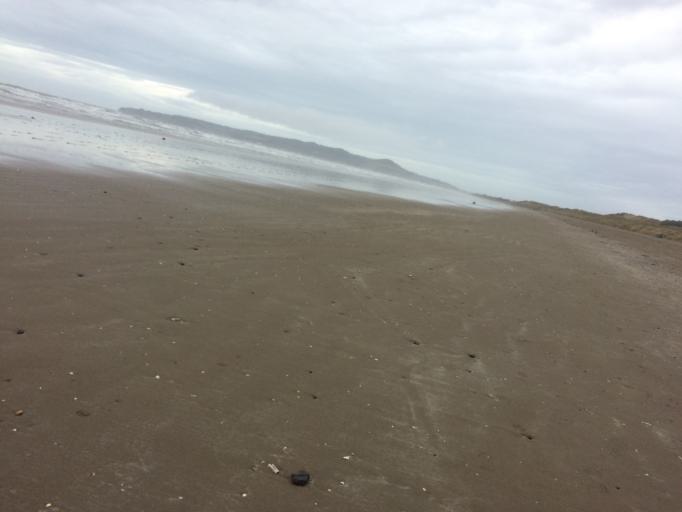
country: IE
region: Leinster
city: Portmarnock
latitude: 53.4240
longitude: -6.1225
